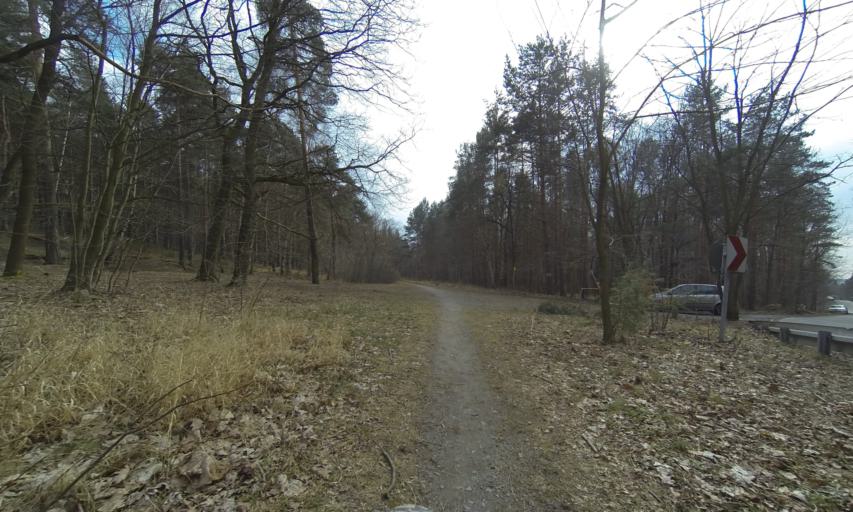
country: DE
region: Saxony
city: Radebeul
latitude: 51.1065
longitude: 13.7159
